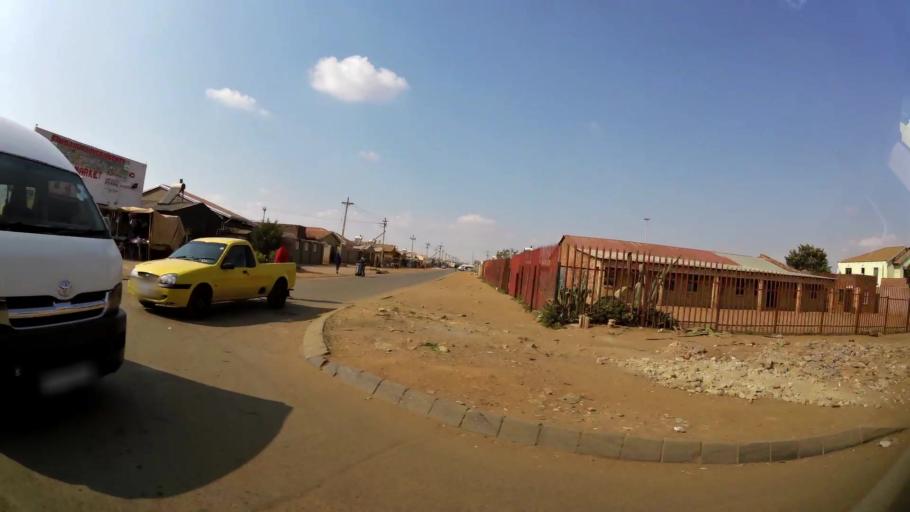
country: ZA
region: Gauteng
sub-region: Ekurhuleni Metropolitan Municipality
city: Springs
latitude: -26.1104
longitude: 28.4771
